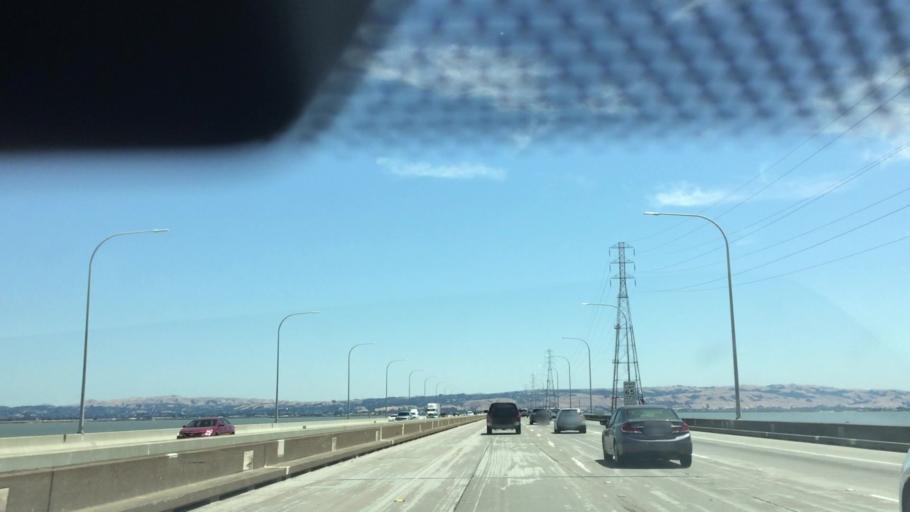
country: US
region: California
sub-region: San Mateo County
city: Foster City
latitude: 37.6049
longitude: -122.1977
